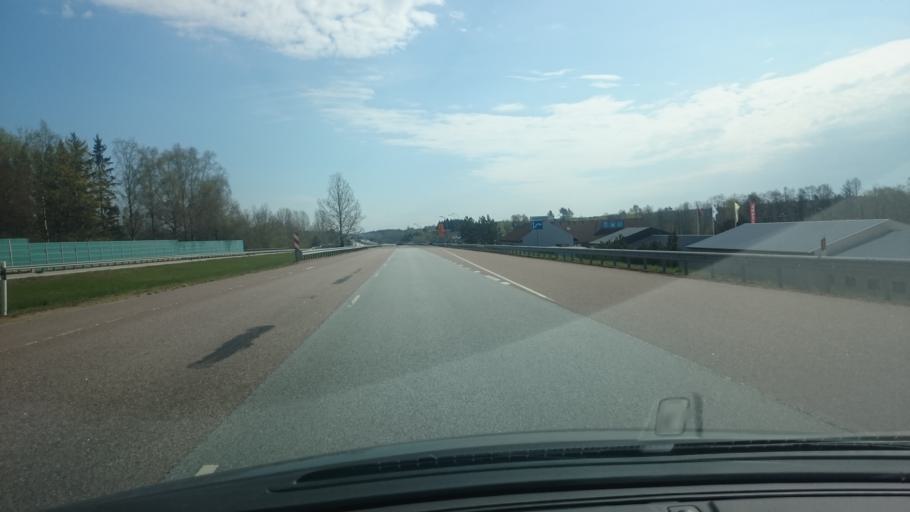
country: EE
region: Harju
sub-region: Kuusalu vald
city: Kuusalu
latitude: 59.4481
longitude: 25.4297
